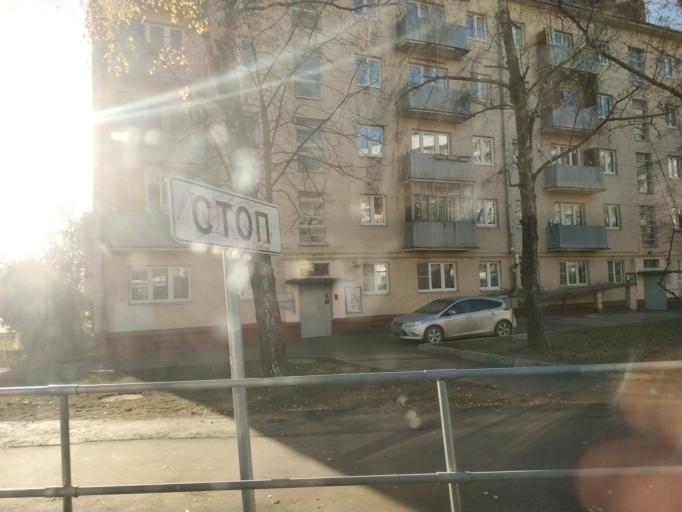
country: RU
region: Moscow
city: Biryulevo
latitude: 55.5807
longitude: 37.6768
